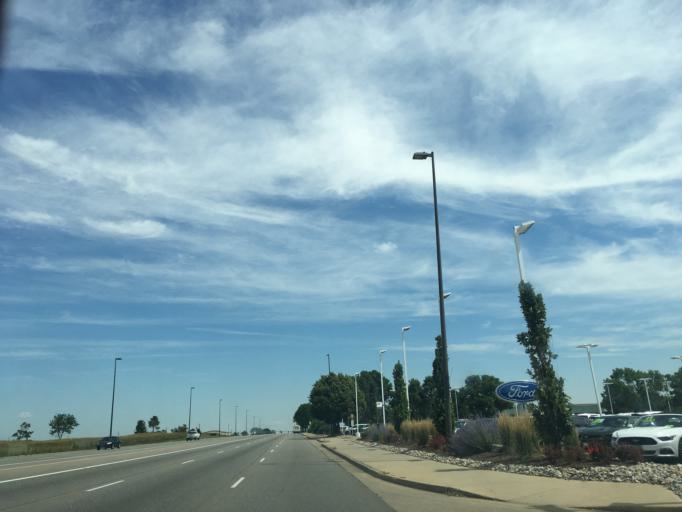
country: US
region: Colorado
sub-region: Adams County
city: Aurora
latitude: 39.7133
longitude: -104.8659
